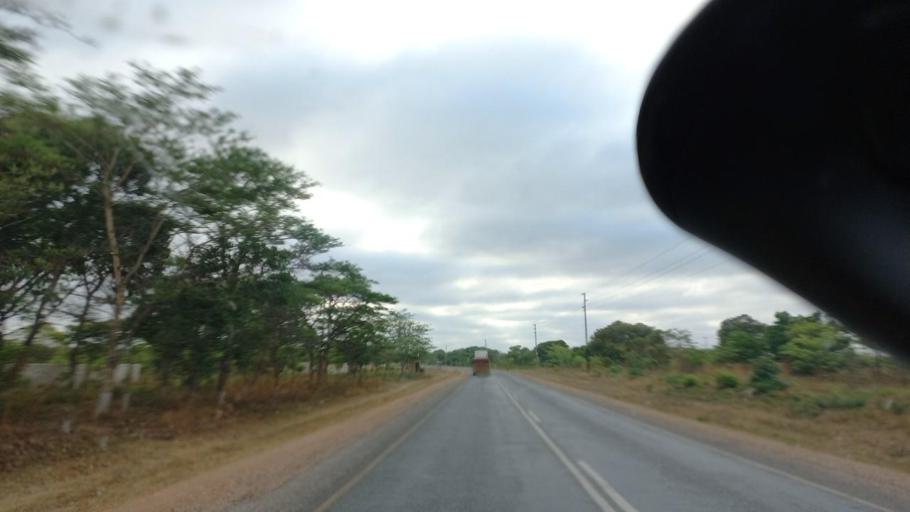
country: ZM
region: Lusaka
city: Chongwe
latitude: -15.3515
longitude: 28.5392
